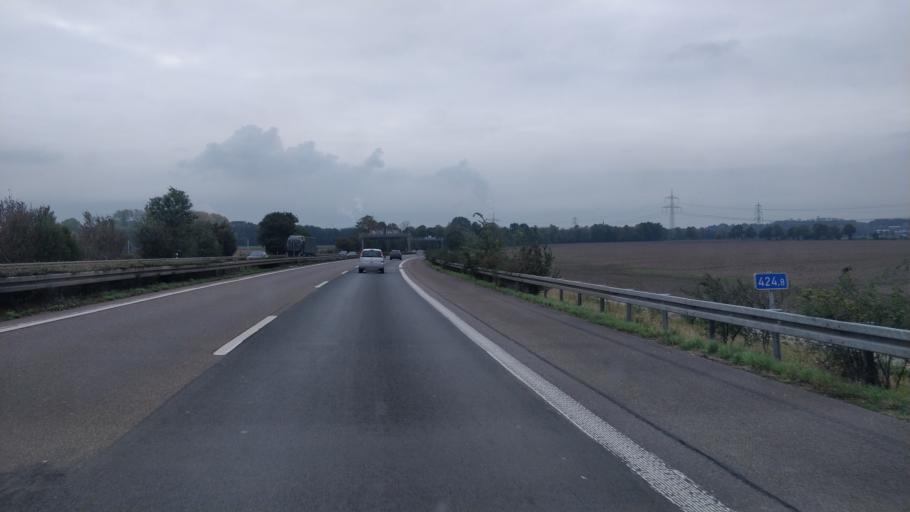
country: DE
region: North Rhine-Westphalia
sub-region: Regierungsbezirk Koln
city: Frechen
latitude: 50.9076
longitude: 6.8471
